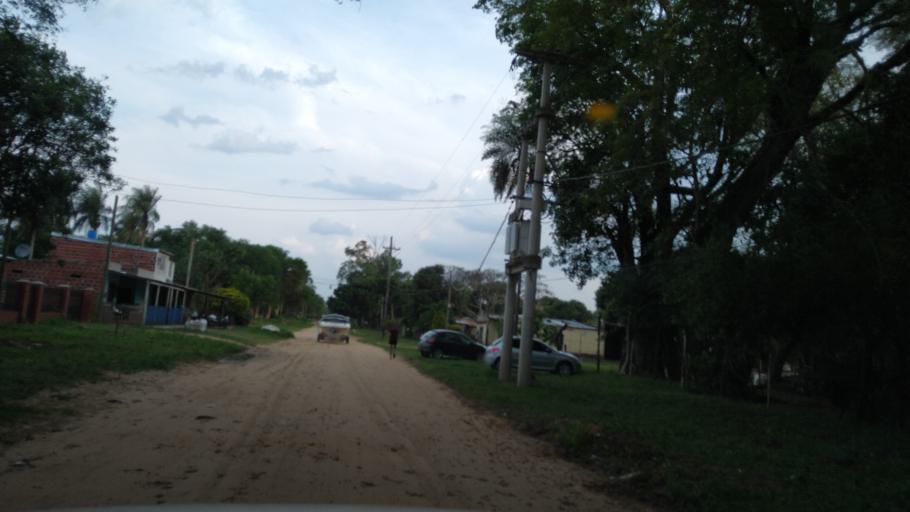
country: AR
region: Corrientes
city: Ituzaingo
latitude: -27.5921
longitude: -56.7056
